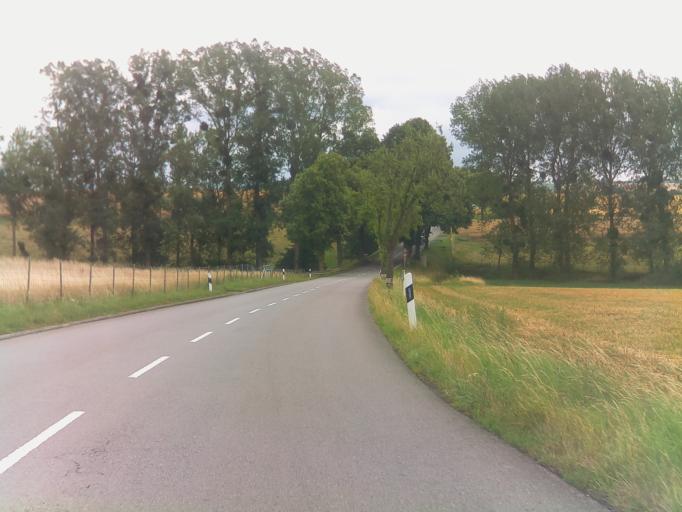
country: LU
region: Grevenmacher
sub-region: Canton de Remich
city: Mondorf-les-Bains
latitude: 49.4945
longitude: 6.2964
